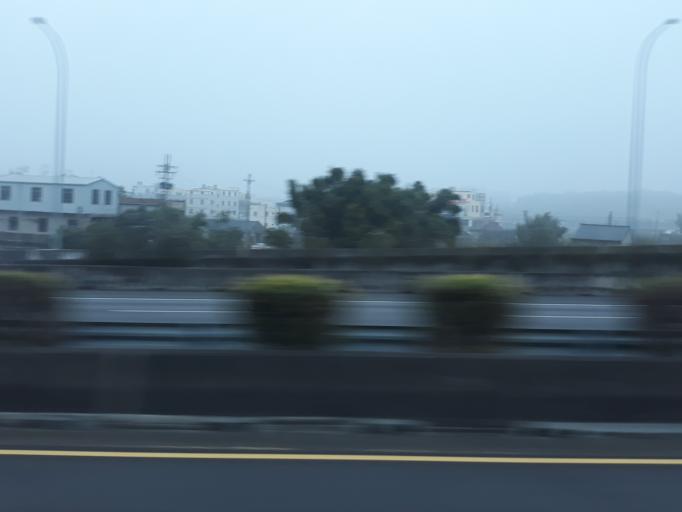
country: TW
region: Taiwan
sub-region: Miaoli
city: Miaoli
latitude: 24.4791
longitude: 120.7837
